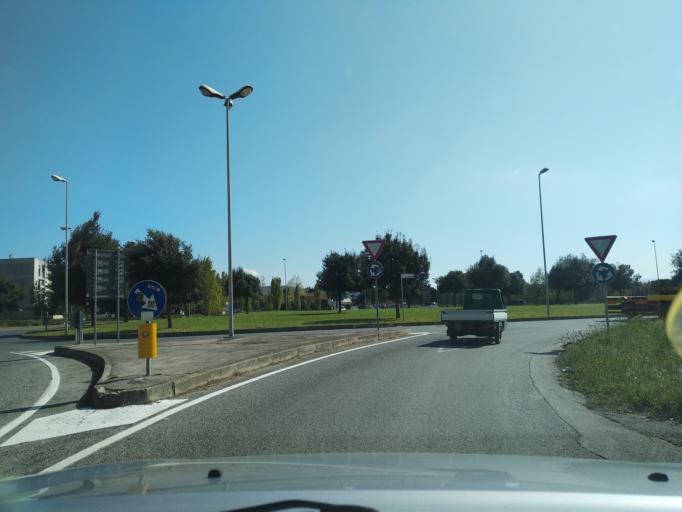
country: IT
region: Tuscany
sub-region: Provincia di Livorno
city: Livorno
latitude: 43.5321
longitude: 10.3423
